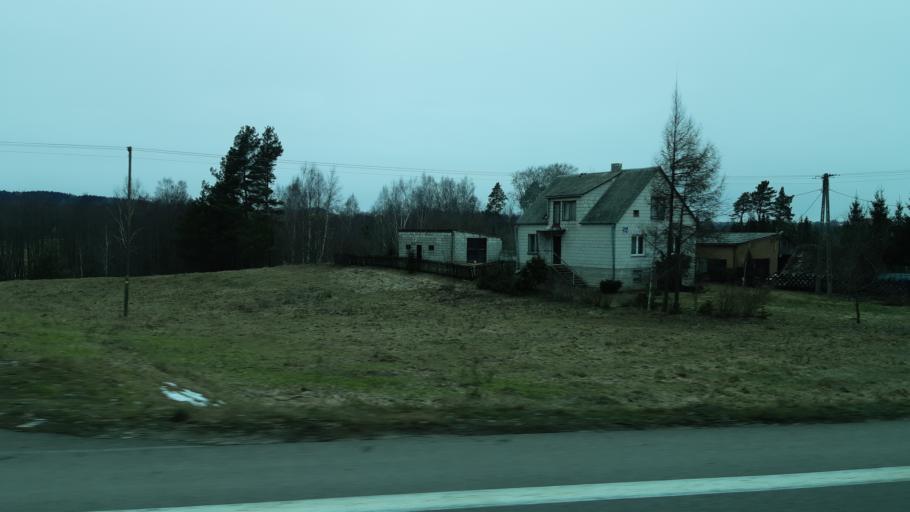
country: PL
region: Podlasie
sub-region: Suwalki
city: Suwalki
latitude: 54.3143
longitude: 22.9607
